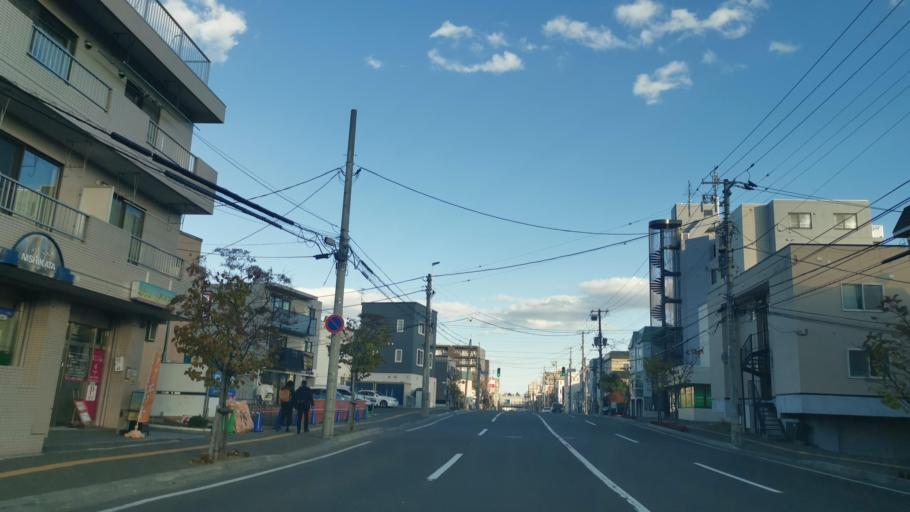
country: JP
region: Hokkaido
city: Sapporo
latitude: 43.0161
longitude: 141.3603
